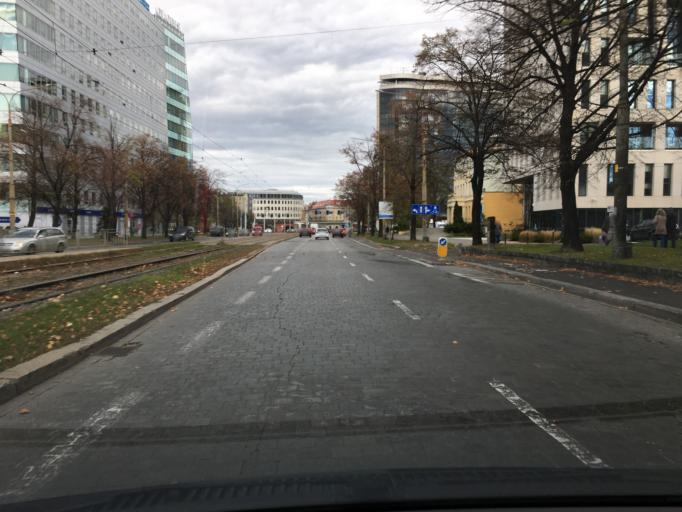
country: PL
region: Lower Silesian Voivodeship
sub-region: Powiat wroclawski
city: Wroclaw
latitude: 51.0979
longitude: 17.0256
